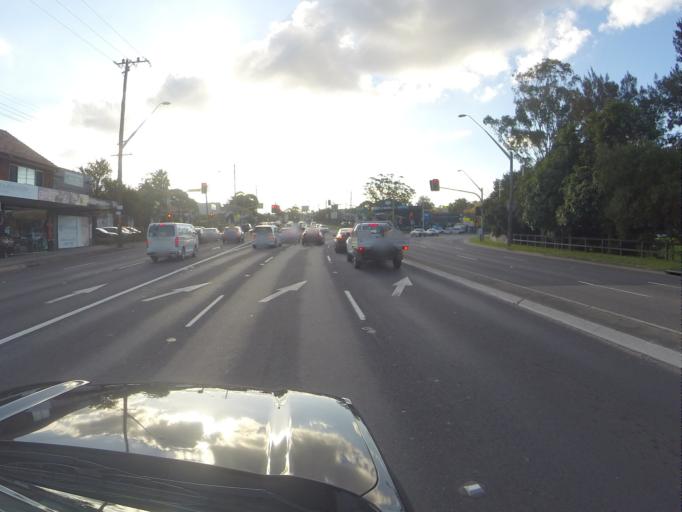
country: AU
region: New South Wales
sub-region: Kogarah
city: Blakehurst
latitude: -33.9884
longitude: 151.1120
